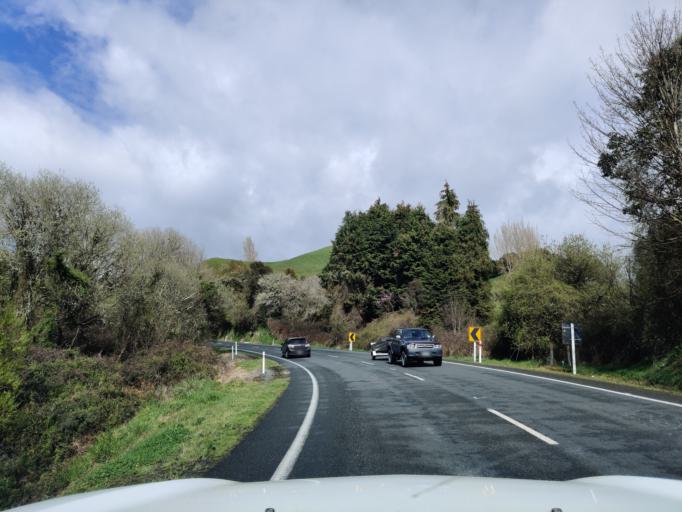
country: NZ
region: Waikato
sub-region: Otorohanga District
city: Otorohanga
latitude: -38.5976
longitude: 175.2176
